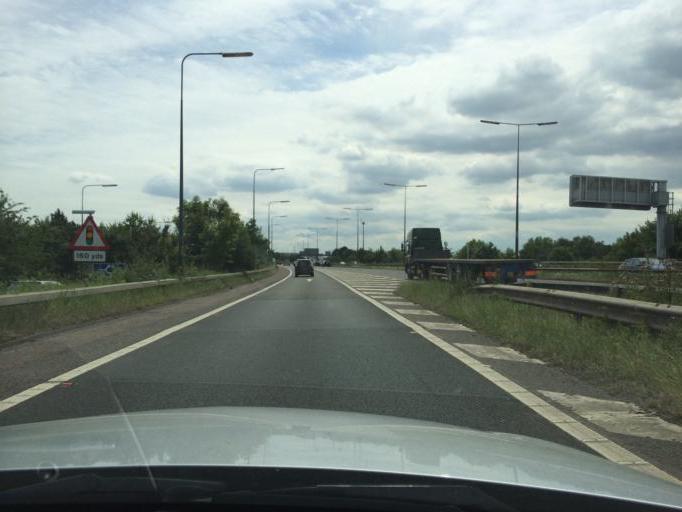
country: GB
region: England
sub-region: Manchester
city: Swinton
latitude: 53.4784
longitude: -2.3746
